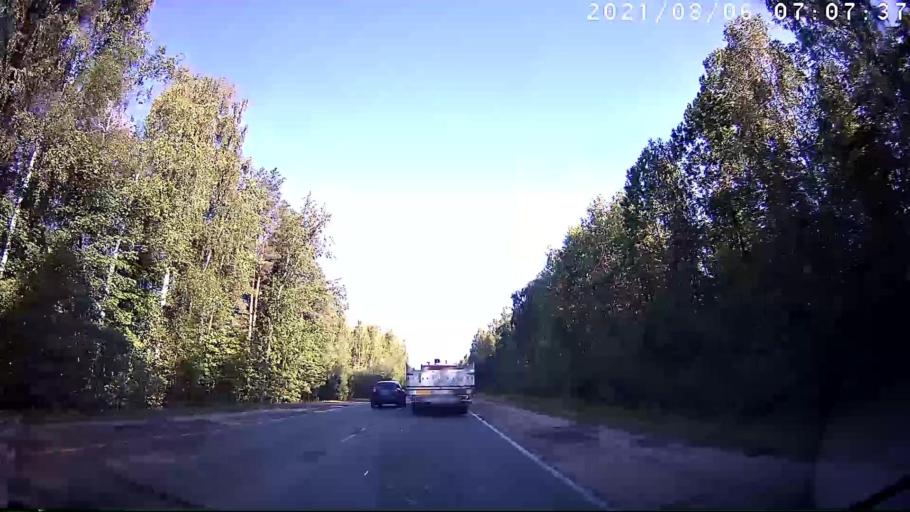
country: RU
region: Mariy-El
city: Yoshkar-Ola
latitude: 56.5644
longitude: 47.9776
